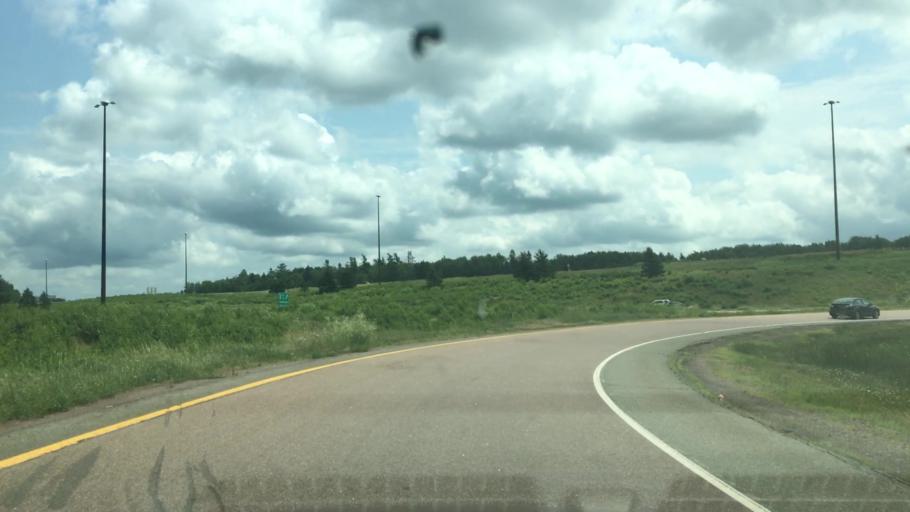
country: CA
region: New Brunswick
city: Dieppe
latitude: 46.1298
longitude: -64.6805
